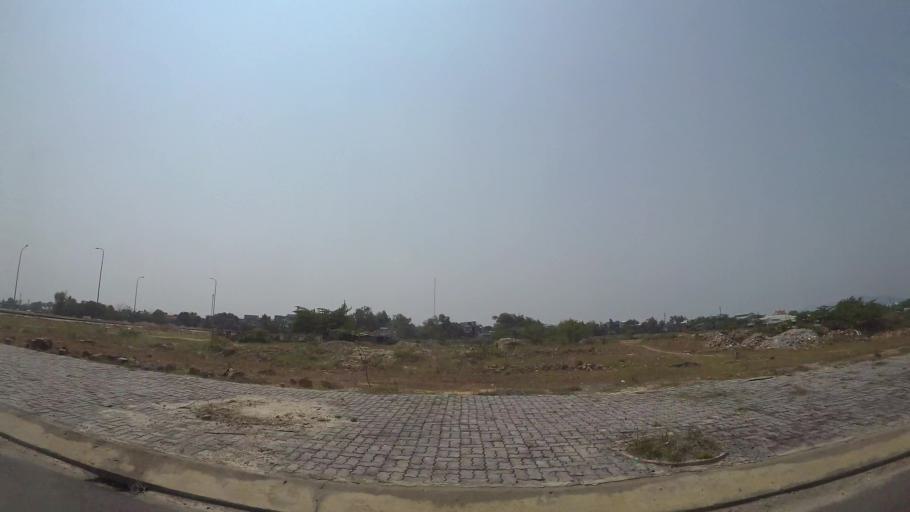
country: VN
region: Da Nang
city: Cam Le
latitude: 15.9780
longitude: 108.2116
